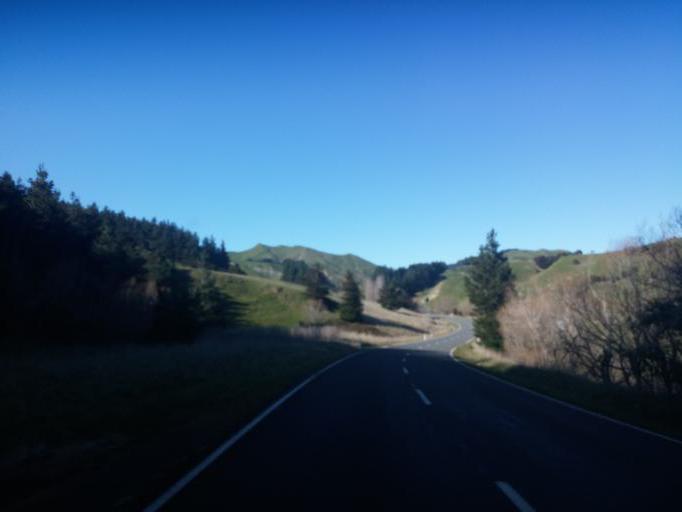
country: NZ
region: Wellington
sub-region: South Wairarapa District
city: Waipawa
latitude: -41.3169
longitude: 175.4732
